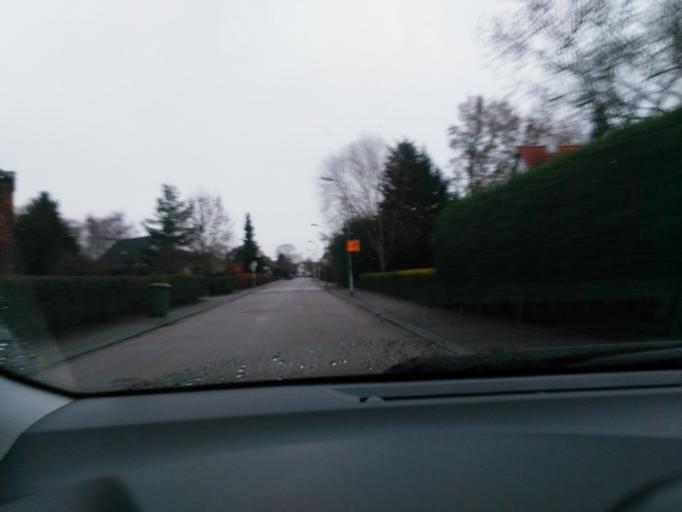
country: NL
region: Zeeland
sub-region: Gemeente Hulst
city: Hulst
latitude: 51.2565
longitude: 4.0610
